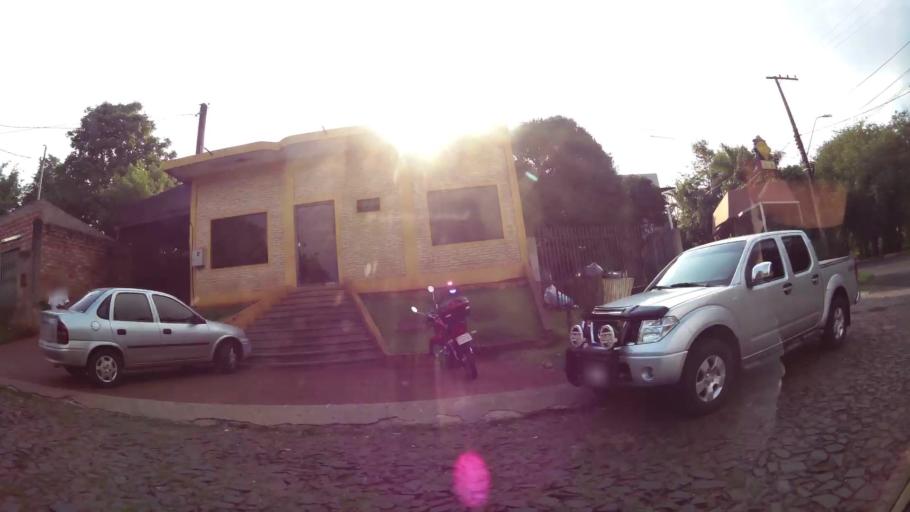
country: PY
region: Alto Parana
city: Presidente Franco
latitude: -25.5247
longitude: -54.6285
